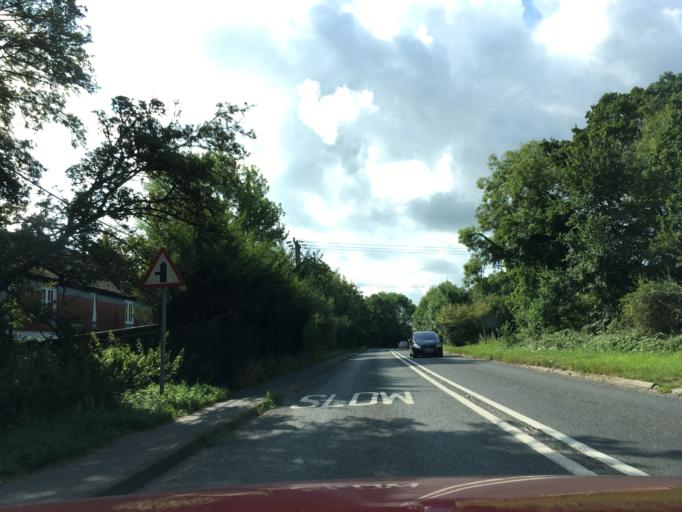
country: GB
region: England
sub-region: Hampshire
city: Bishops Waltham
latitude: 50.9471
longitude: -1.2042
